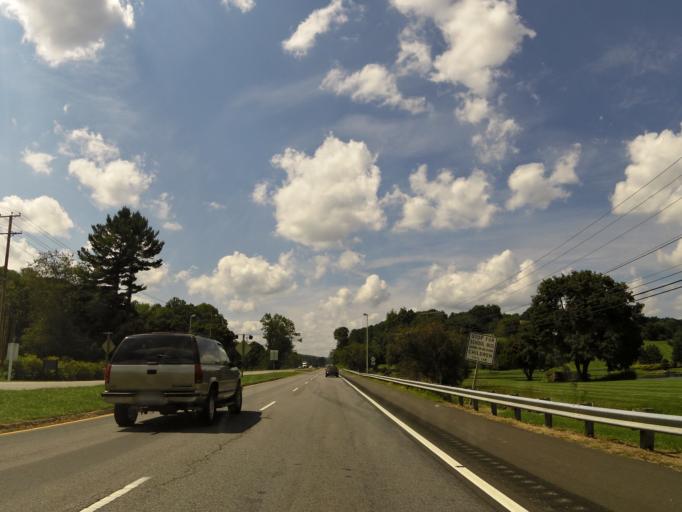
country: US
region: Virginia
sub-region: Washington County
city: Abingdon
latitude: 36.7141
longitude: -81.9998
